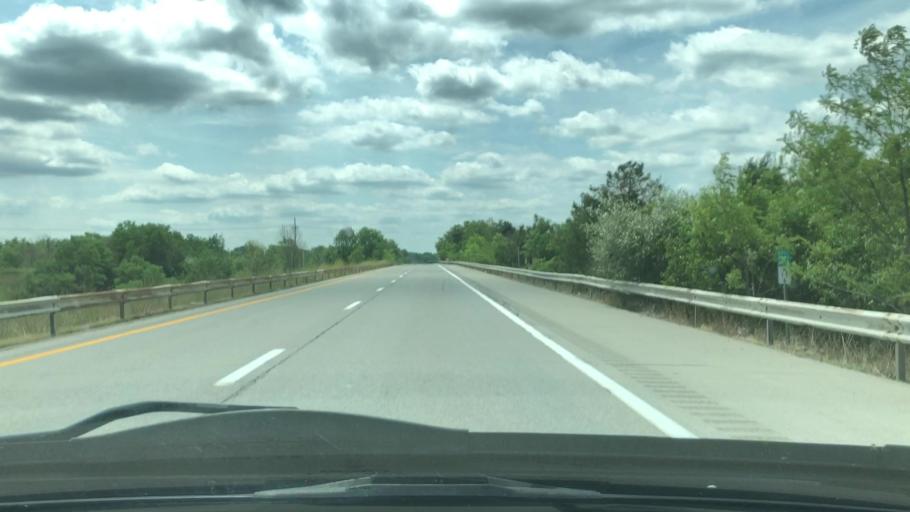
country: US
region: New York
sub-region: Monroe County
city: Spencerport
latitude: 43.1033
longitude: -77.7871
